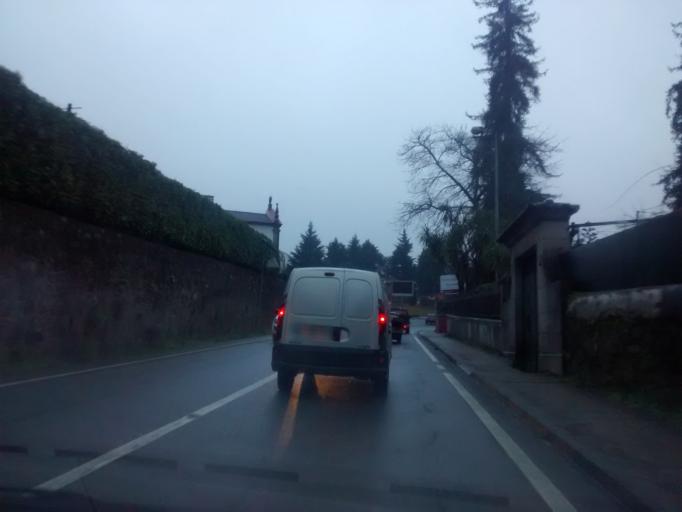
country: PT
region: Braga
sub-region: Braga
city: Braga
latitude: 41.5589
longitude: -8.4184
